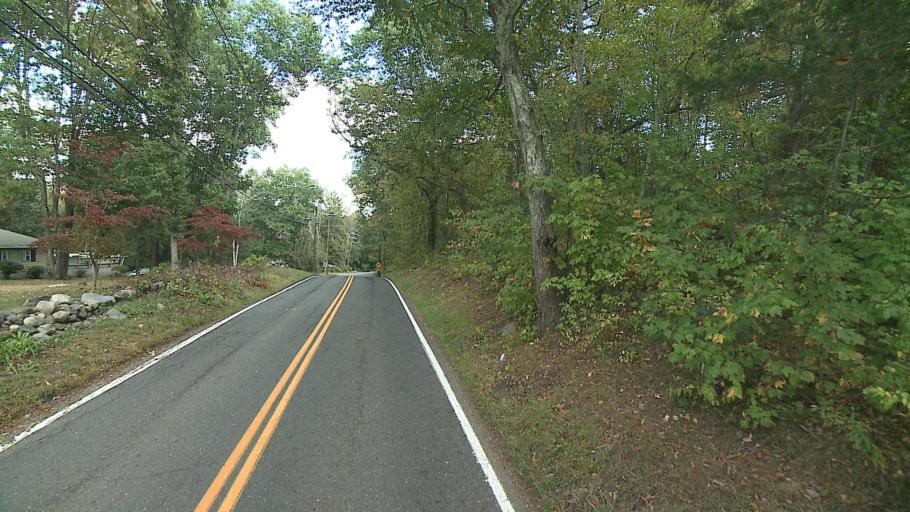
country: US
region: Connecticut
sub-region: New Haven County
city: Oxford
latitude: 41.4356
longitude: -73.0898
